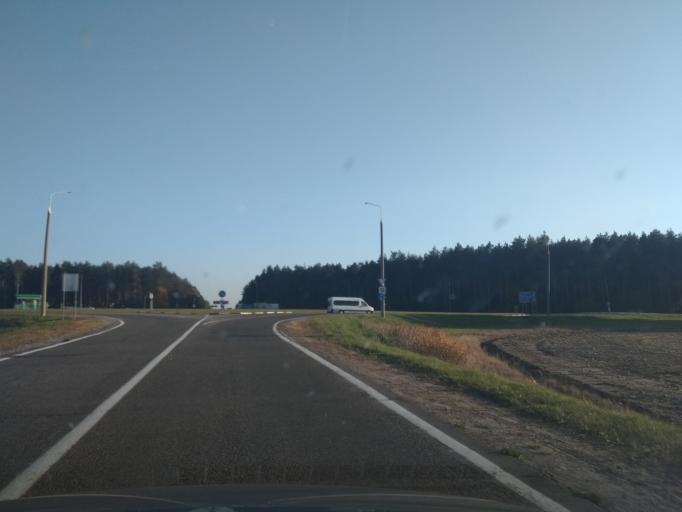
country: BY
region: Grodnenskaya
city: Vawkavysk
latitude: 53.1462
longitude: 24.5039
